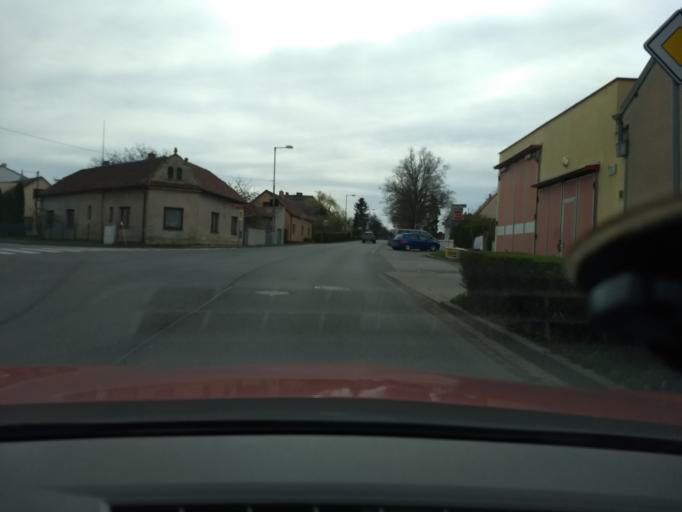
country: CZ
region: Central Bohemia
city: Horomerice
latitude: 50.1310
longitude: 14.3406
